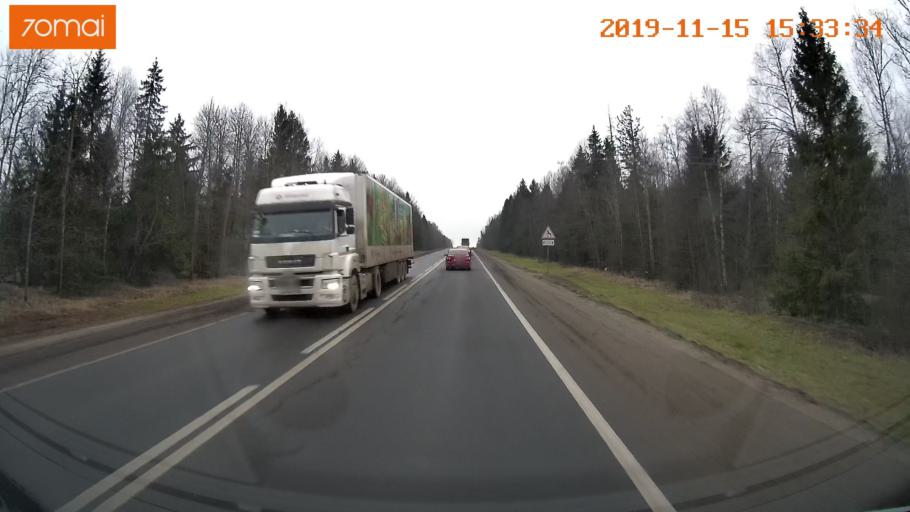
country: RU
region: Jaroslavl
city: Danilov
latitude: 58.0791
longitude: 40.0922
